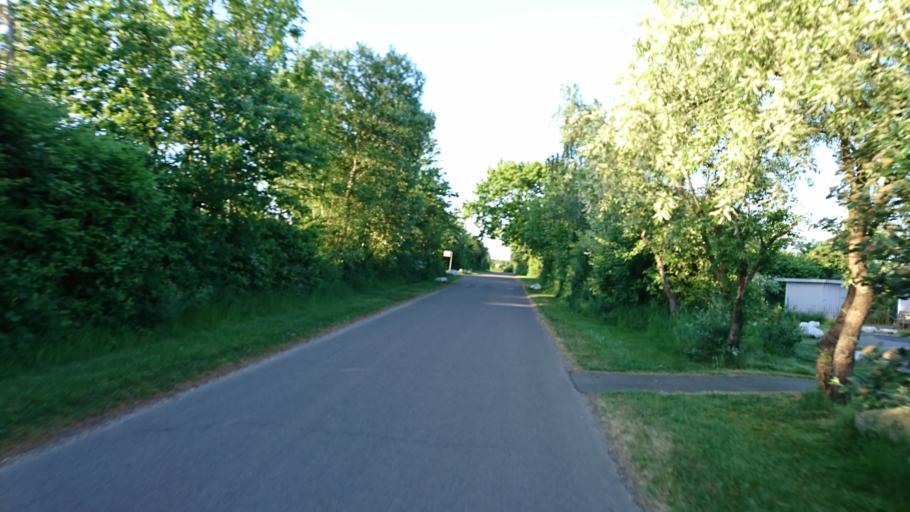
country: DK
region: Capital Region
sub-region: Ballerup Kommune
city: Ballerup
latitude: 55.7156
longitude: 12.3335
